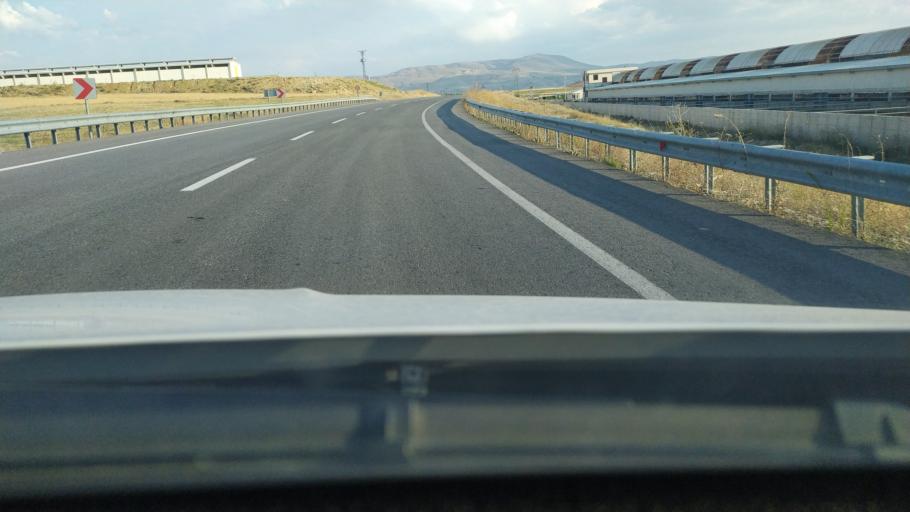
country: TR
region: Kayseri
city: Bunyan
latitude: 38.9141
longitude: 35.7539
